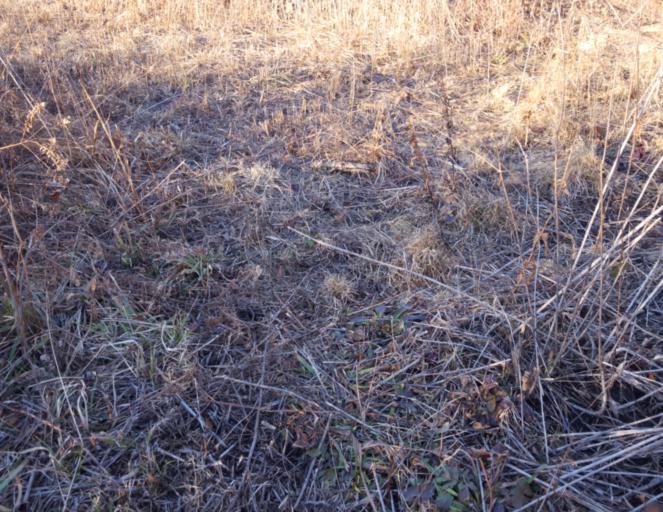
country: US
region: Illinois
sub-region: Cook County
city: Northbrook
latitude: 42.1411
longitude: -87.8282
